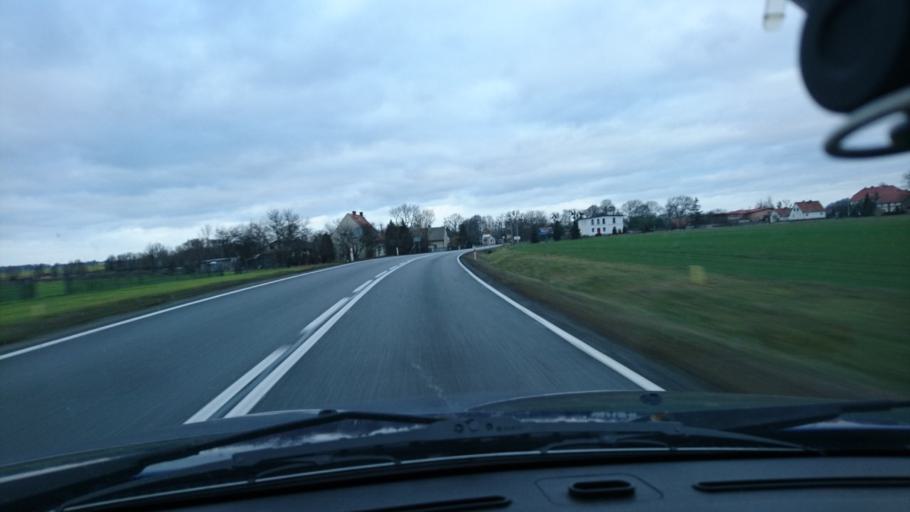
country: PL
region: Opole Voivodeship
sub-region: Powiat kluczborski
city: Byczyna
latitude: 51.0593
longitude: 18.1992
